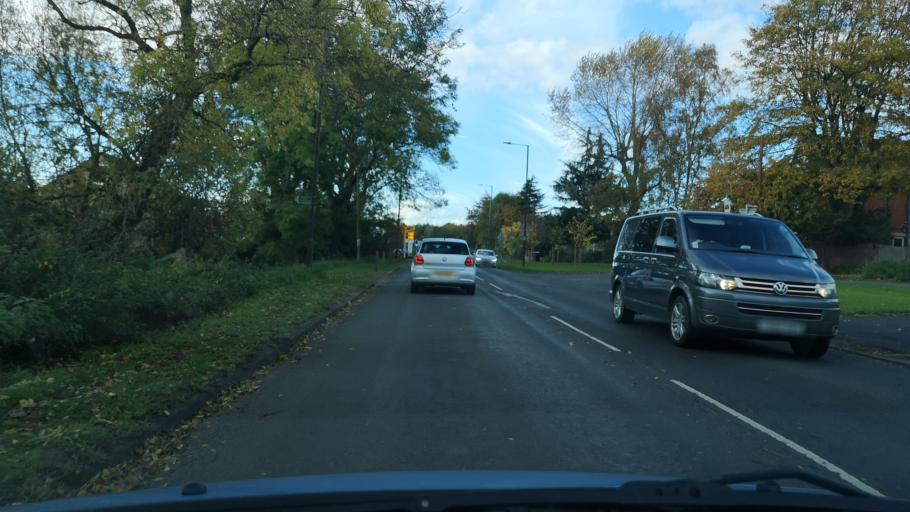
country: GB
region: England
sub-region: Doncaster
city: Hatfield
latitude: 53.6157
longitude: -0.9733
